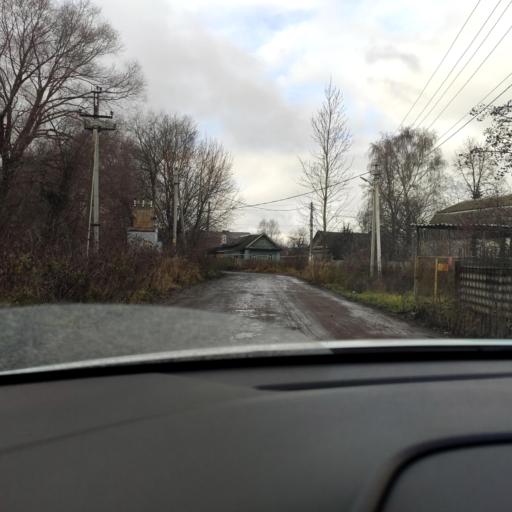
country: RU
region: Tatarstan
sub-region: Gorod Kazan'
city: Kazan
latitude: 55.8813
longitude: 49.0953
